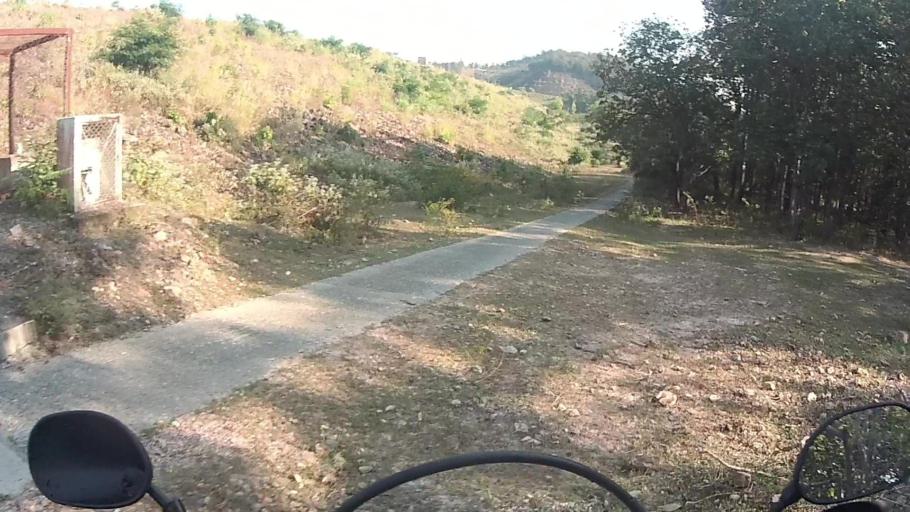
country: TH
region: Chiang Mai
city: San Sai
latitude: 18.9270
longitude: 99.1129
